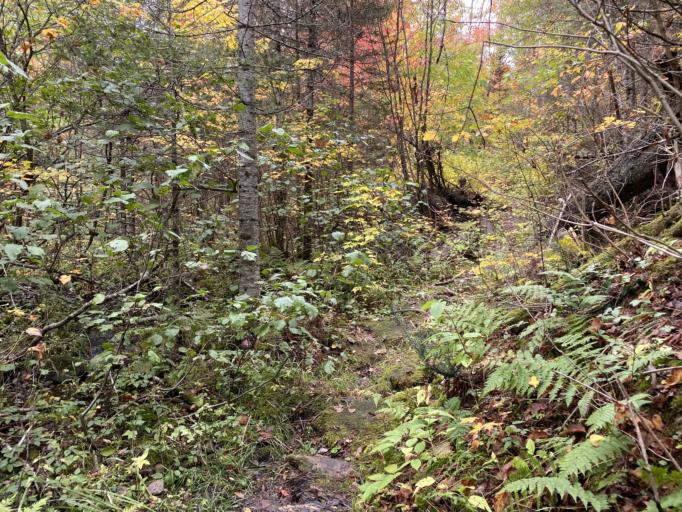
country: US
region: Michigan
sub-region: Marquette County
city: West Ishpeming
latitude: 46.5413
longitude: -87.9987
